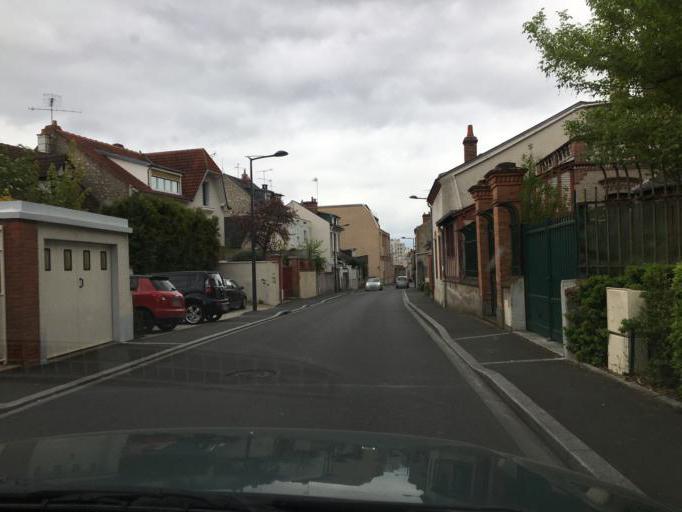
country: FR
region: Centre
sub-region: Departement du Loiret
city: Orleans
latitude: 47.9058
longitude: 1.8870
